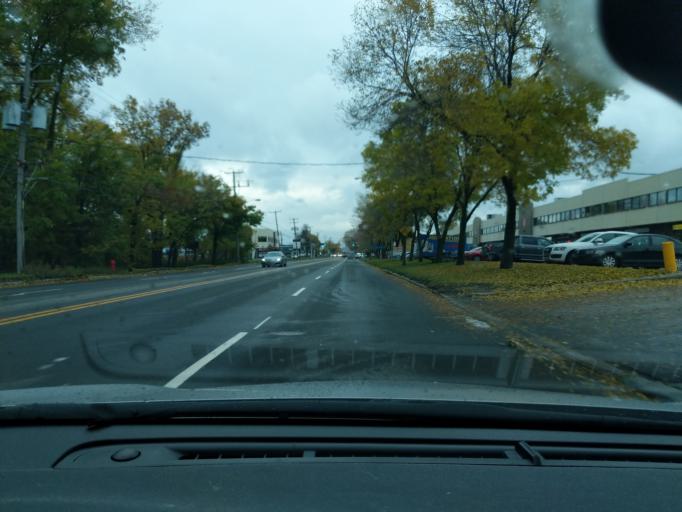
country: CA
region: Quebec
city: L'Ancienne-Lorette
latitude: 46.8062
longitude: -71.3072
